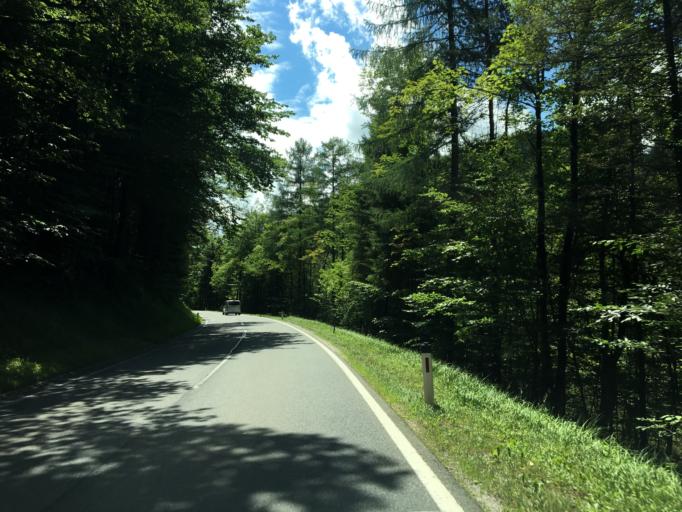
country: AT
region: Salzburg
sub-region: Politischer Bezirk Hallein
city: Adnet
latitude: 47.7224
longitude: 13.1382
